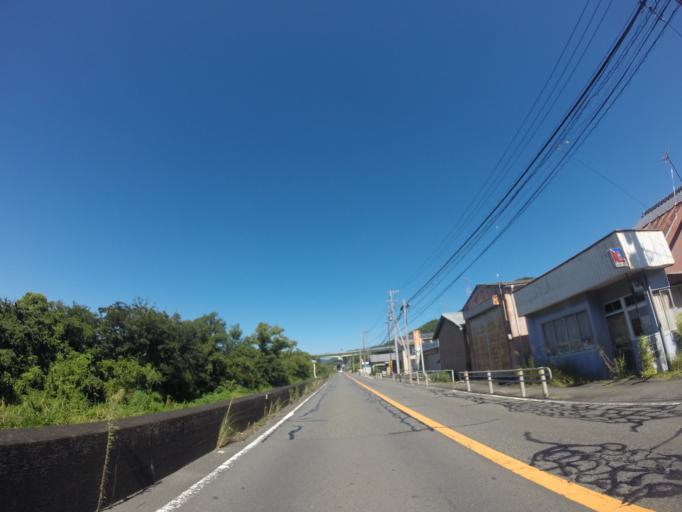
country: JP
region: Shizuoka
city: Kanaya
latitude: 34.8516
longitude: 138.1402
